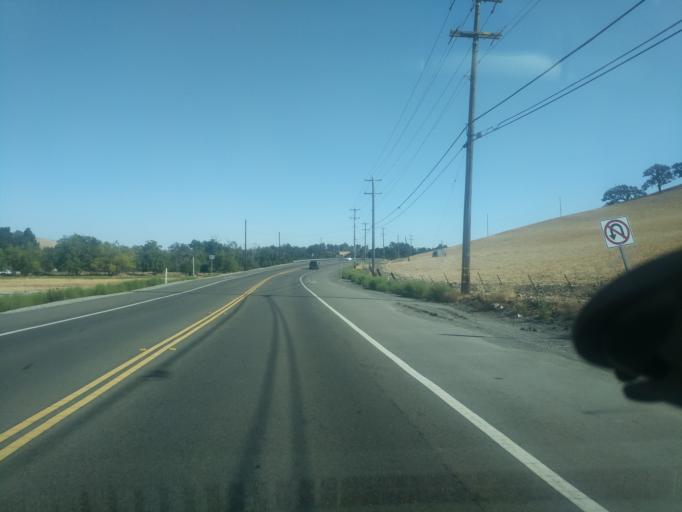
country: US
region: California
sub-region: Contra Costa County
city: Blackhawk
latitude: 37.7968
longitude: -121.8679
